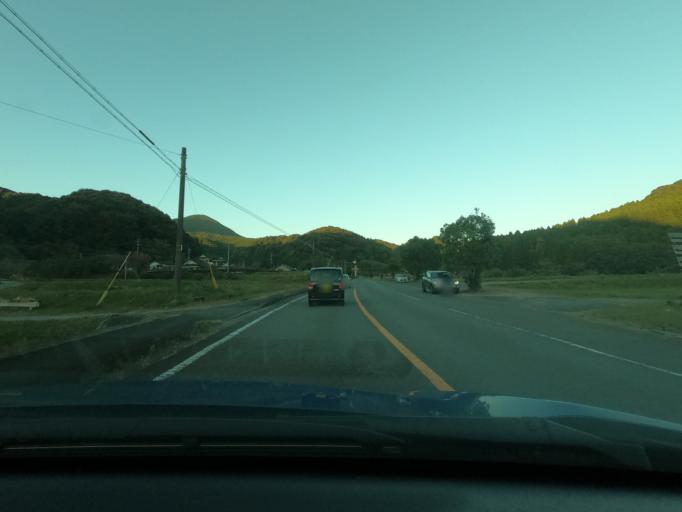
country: JP
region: Kagoshima
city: Satsumasendai
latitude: 31.7940
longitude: 130.4722
